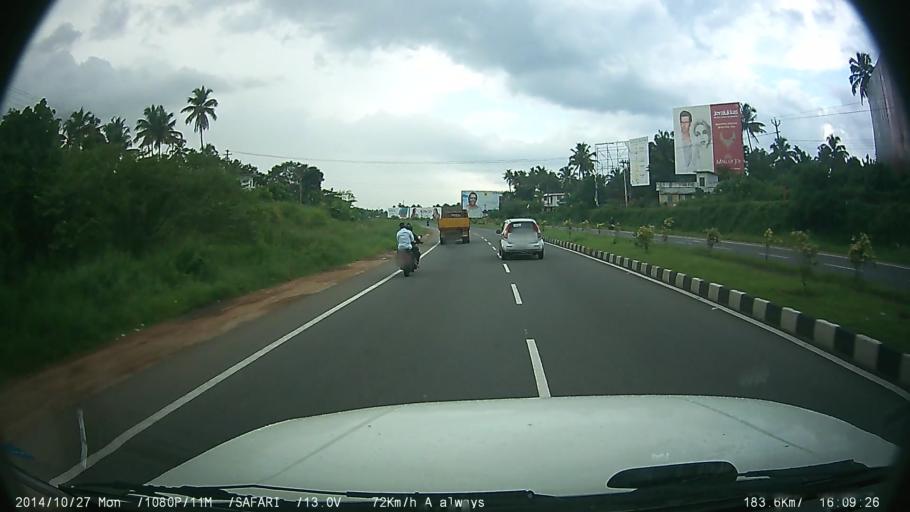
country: IN
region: Kerala
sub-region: Thrissur District
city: Kizhake Chalakudi
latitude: 10.3805
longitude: 76.2974
